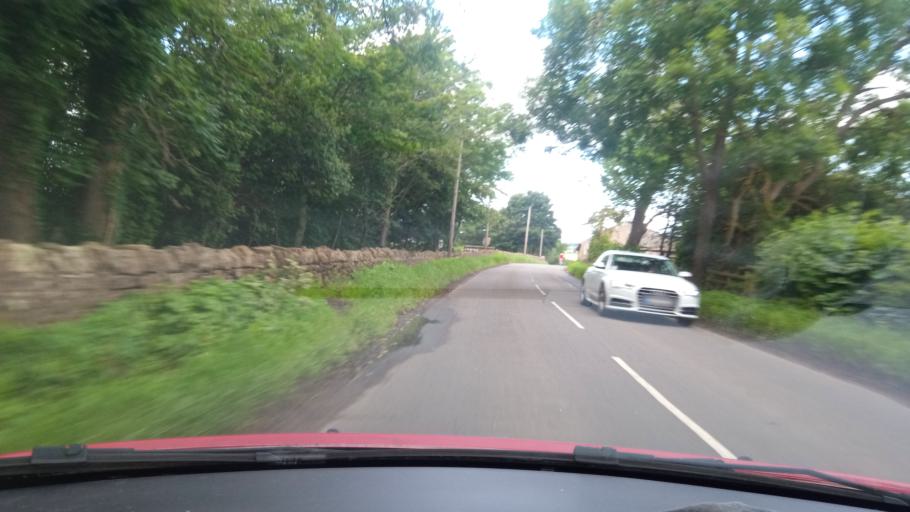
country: GB
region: Scotland
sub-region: East Lothian
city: Pencaitland
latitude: 55.9087
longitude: -2.8565
